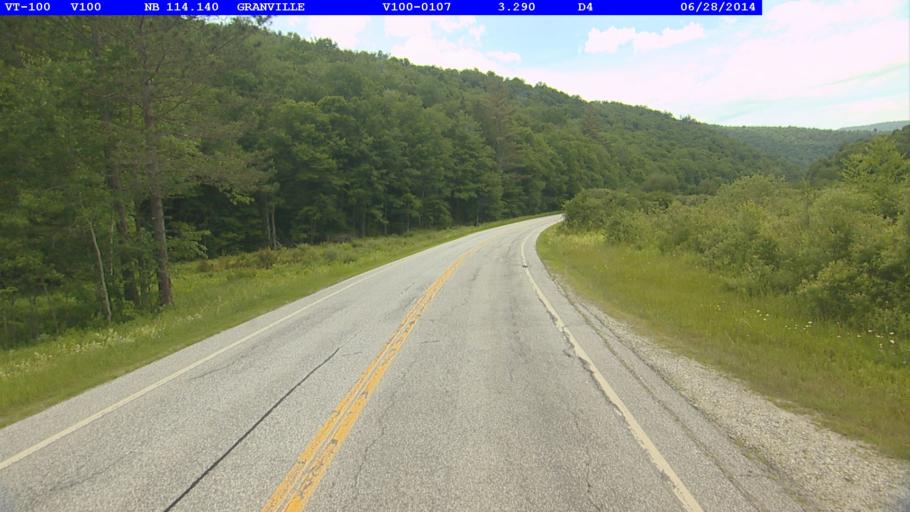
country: US
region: Vermont
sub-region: Orange County
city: Randolph
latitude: 43.9890
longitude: -72.8513
